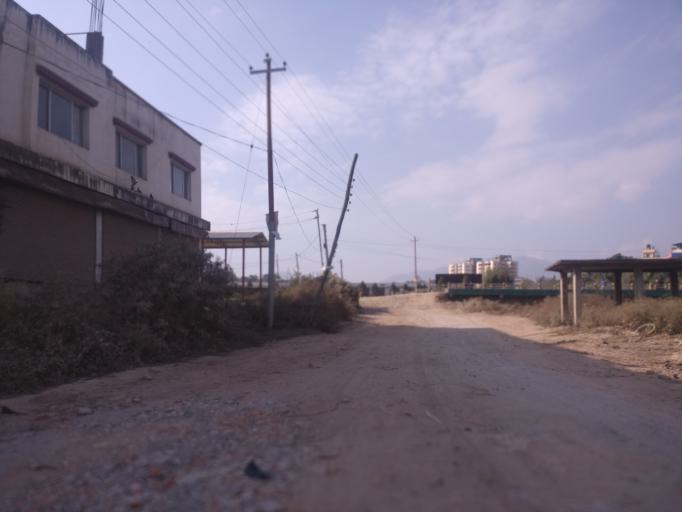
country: NP
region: Central Region
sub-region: Bagmati Zone
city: Patan
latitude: 27.6769
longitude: 85.3360
